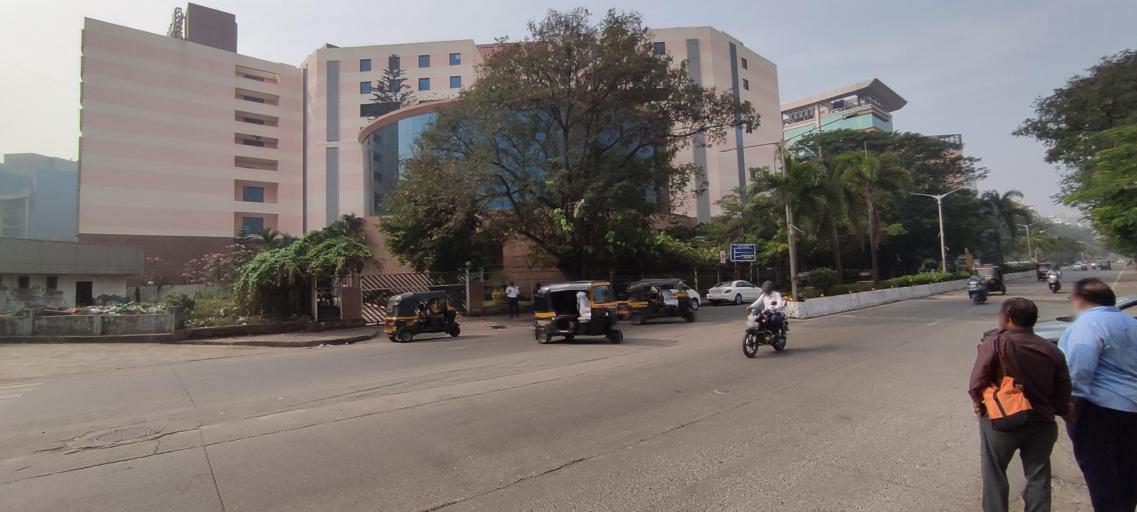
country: IN
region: Maharashtra
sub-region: Mumbai Suburban
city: Mumbai
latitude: 19.0659
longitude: 72.8613
